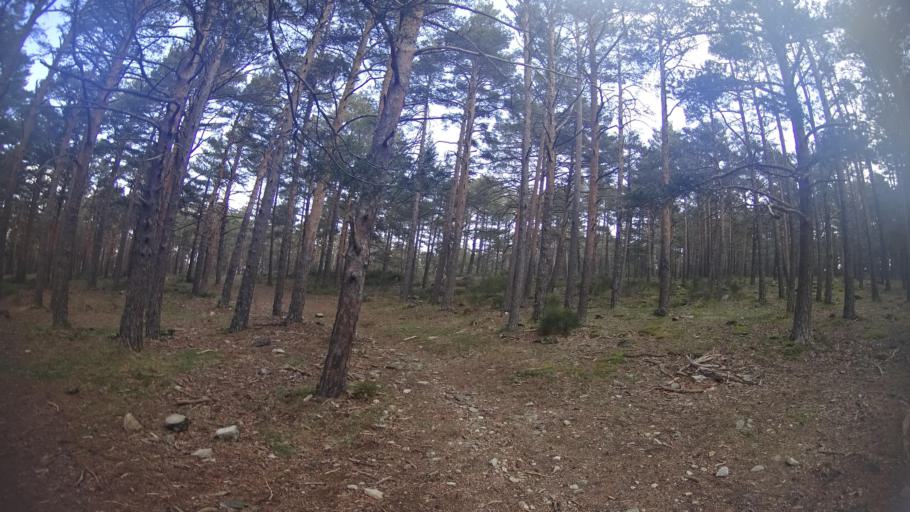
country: ES
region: Madrid
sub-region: Provincia de Madrid
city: Canencia
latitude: 40.8734
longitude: -3.7661
